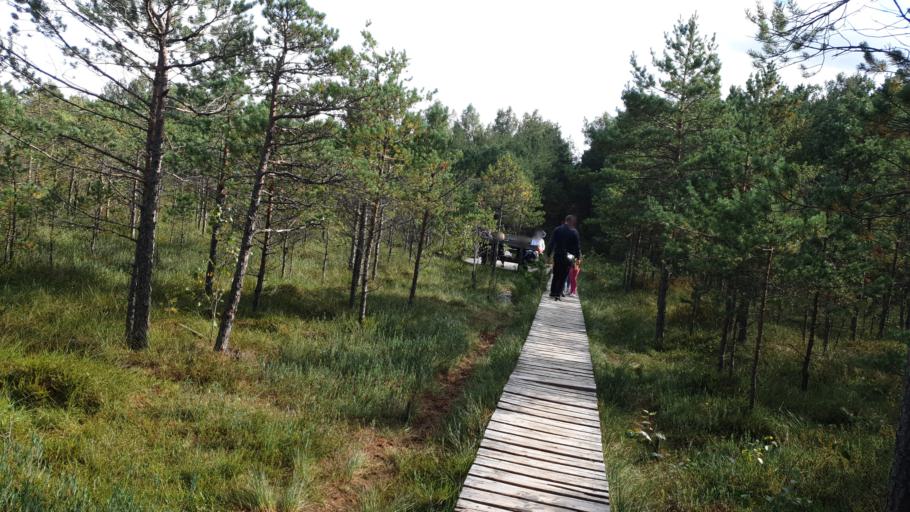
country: LT
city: Trakai
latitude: 54.6424
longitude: 24.9681
